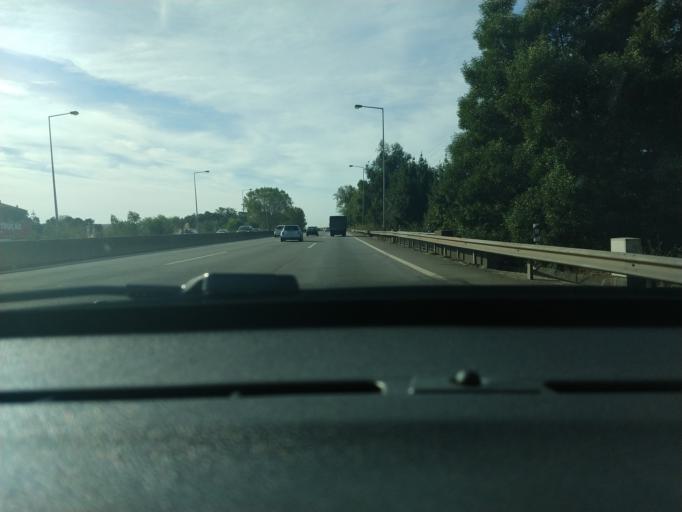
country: PT
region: Porto
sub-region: Vila Nova de Gaia
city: Canidelo
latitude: 41.1260
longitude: -8.6359
